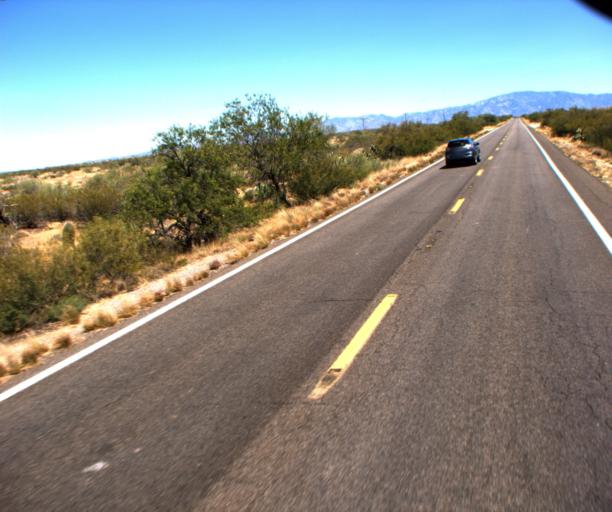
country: US
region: Arizona
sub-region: Pima County
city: Catalina
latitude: 32.6421
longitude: -111.0161
